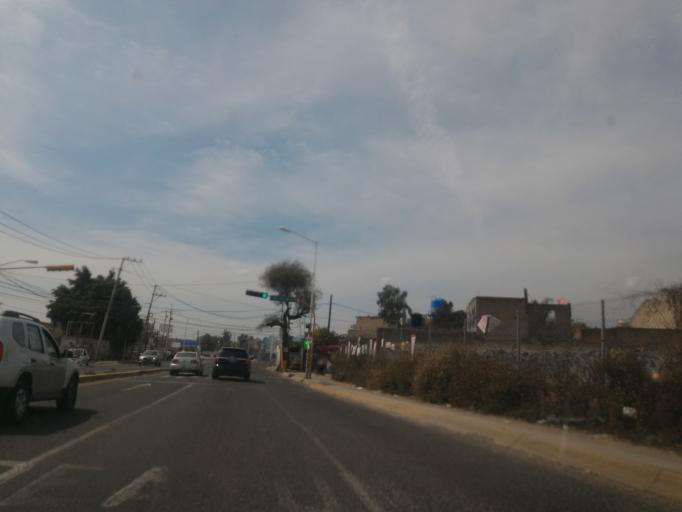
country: MX
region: Jalisco
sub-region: Tlajomulco de Zuniga
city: La Tijera
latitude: 20.5948
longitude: -103.4097
